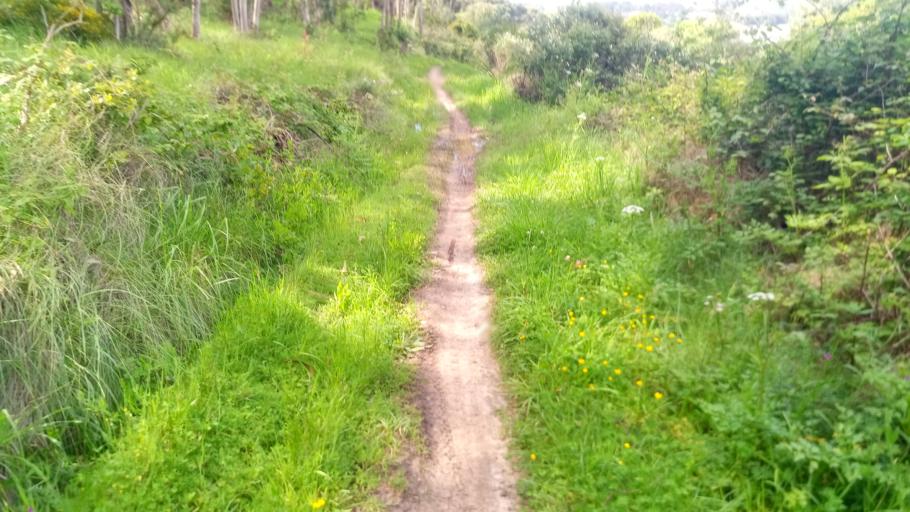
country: PT
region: Leiria
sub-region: Caldas da Rainha
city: Caldas da Rainha
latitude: 39.3999
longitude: -9.1883
